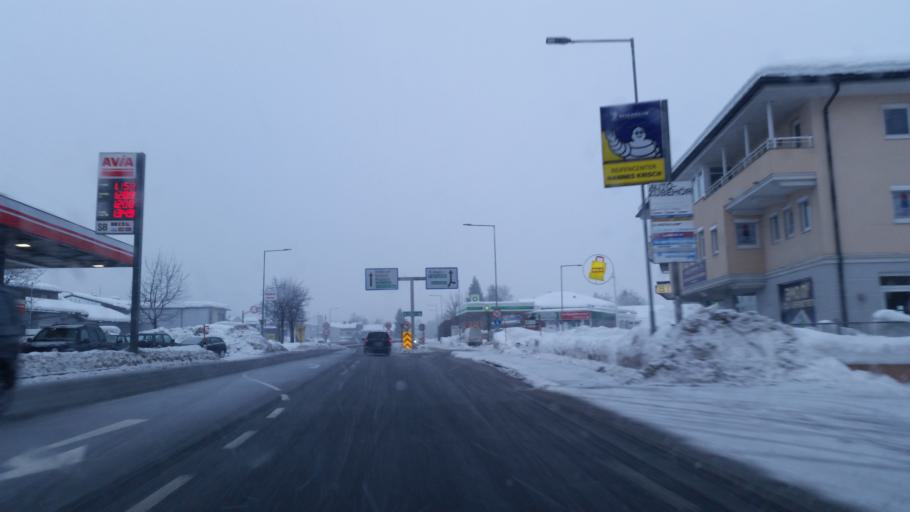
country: AT
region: Tyrol
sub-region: Politischer Bezirk Kitzbuhel
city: Sankt Johann in Tirol
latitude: 47.5261
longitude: 12.4239
